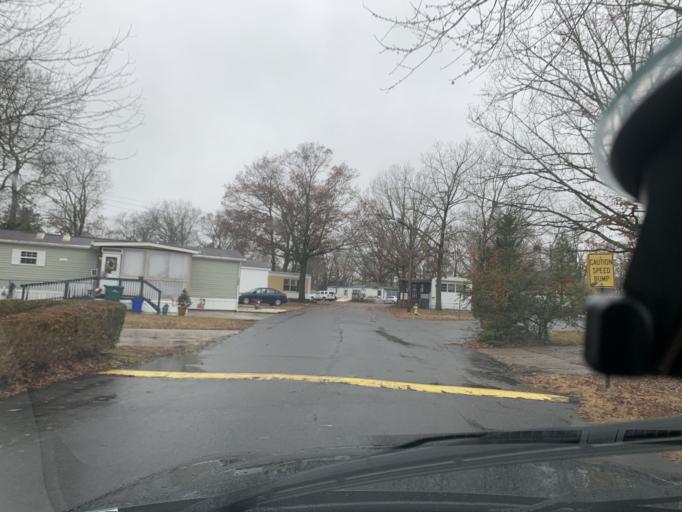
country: US
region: New Jersey
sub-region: Atlantic County
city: Pomona
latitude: 39.4325
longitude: -74.5832
